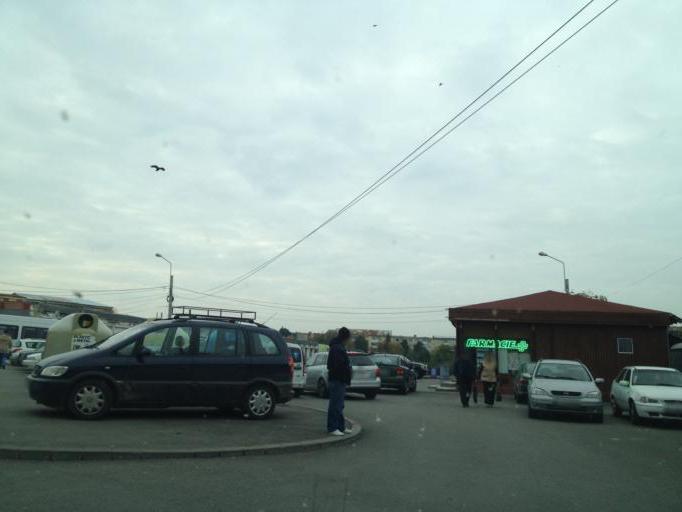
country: RO
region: Dolj
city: Craiova
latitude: 44.3014
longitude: 23.7972
